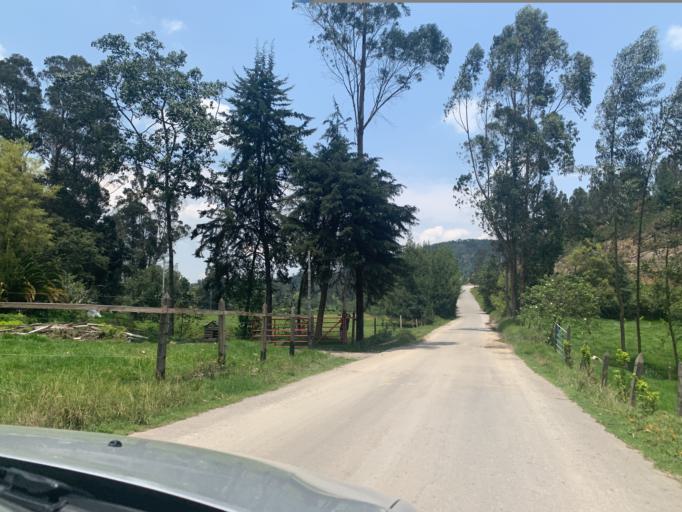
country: CO
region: Boyaca
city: Chiquinquira
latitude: 5.5501
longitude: -73.7514
